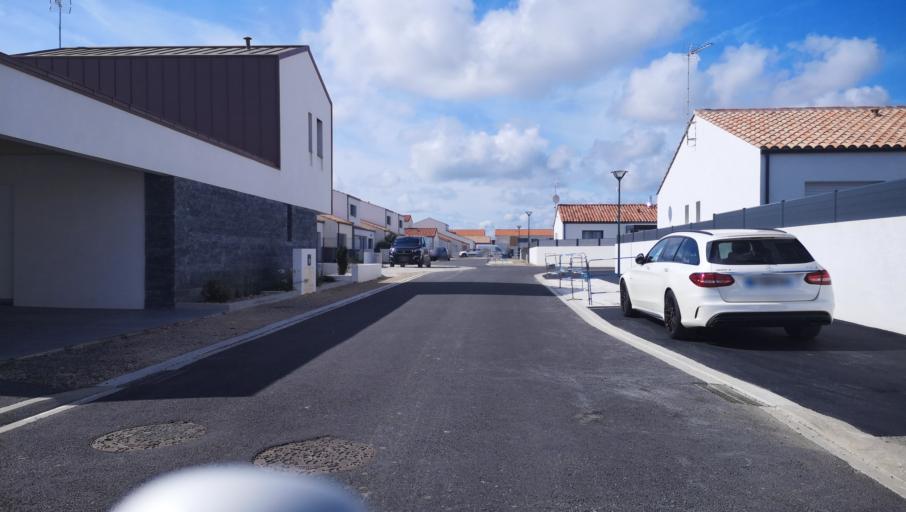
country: FR
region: Pays de la Loire
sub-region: Departement de la Vendee
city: Les Sables-d'Olonne
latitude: 46.5103
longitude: -1.7902
